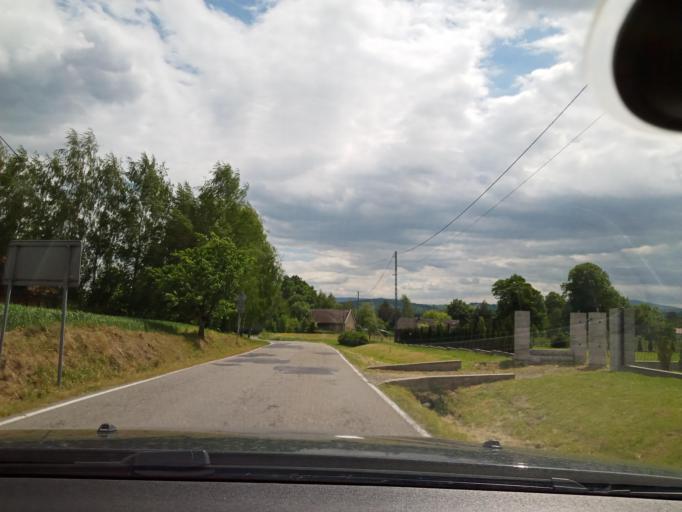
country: PL
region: Lesser Poland Voivodeship
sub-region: Powiat bochenski
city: Lapanow
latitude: 49.8591
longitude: 20.2513
